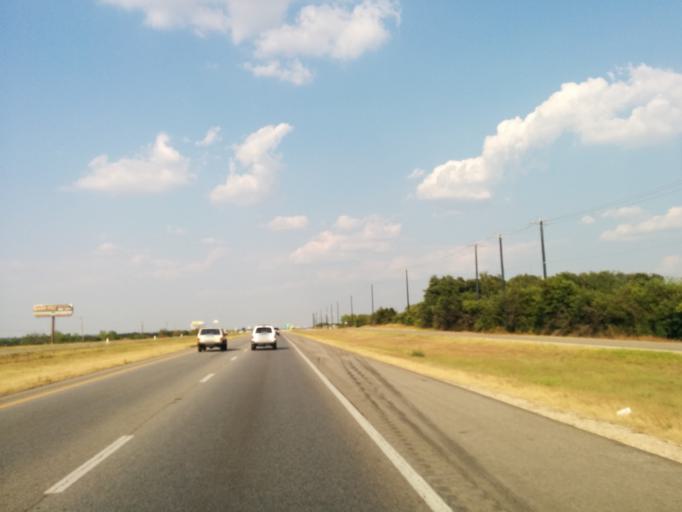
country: US
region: Texas
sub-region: Guadalupe County
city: Cibolo
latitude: 29.4848
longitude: -98.2324
